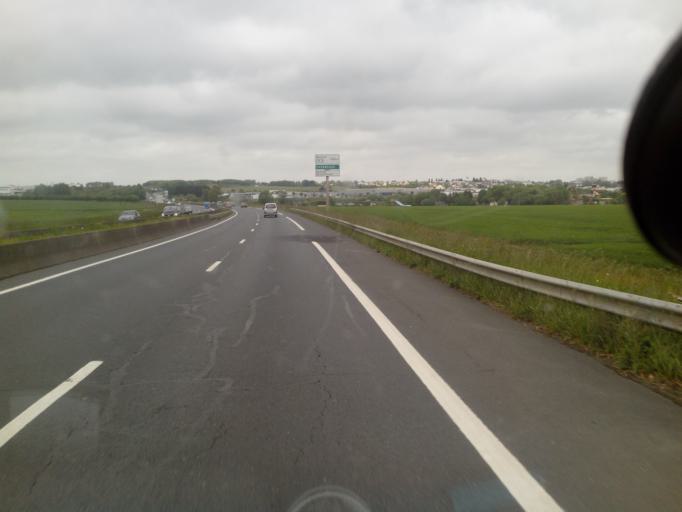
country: FR
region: Lower Normandy
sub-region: Departement du Calvados
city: Bretteville-sur-Odon
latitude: 49.1770
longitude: -0.4284
